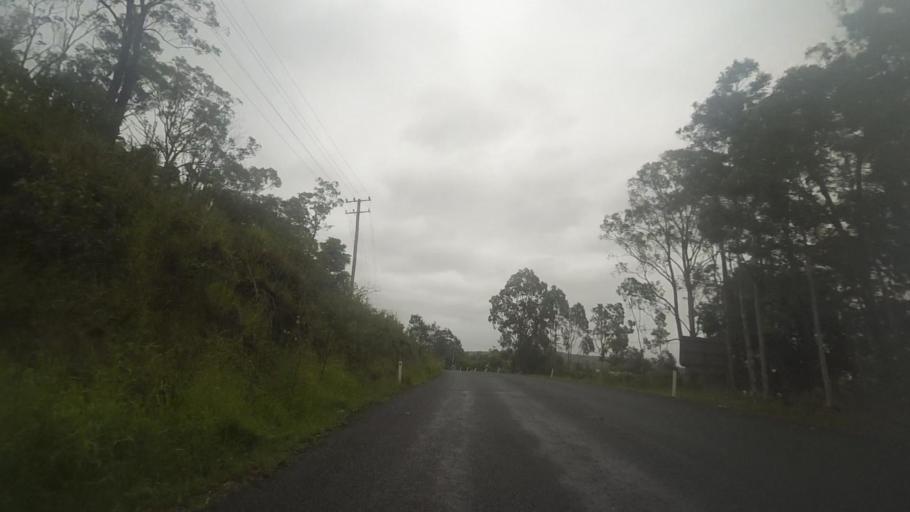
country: AU
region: New South Wales
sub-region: Port Stephens Shire
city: Port Stephens
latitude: -32.6501
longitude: 151.9733
